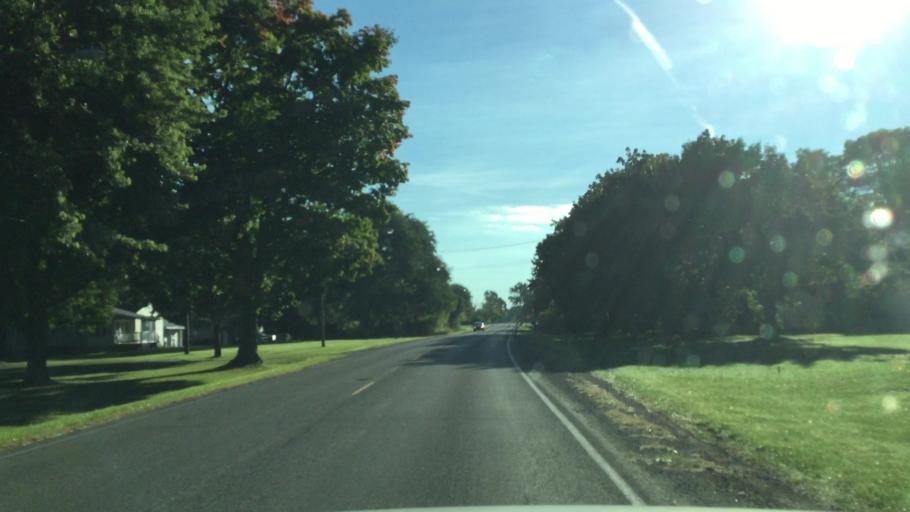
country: US
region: Michigan
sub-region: Genesee County
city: Beecher
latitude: 43.0900
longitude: -83.7439
